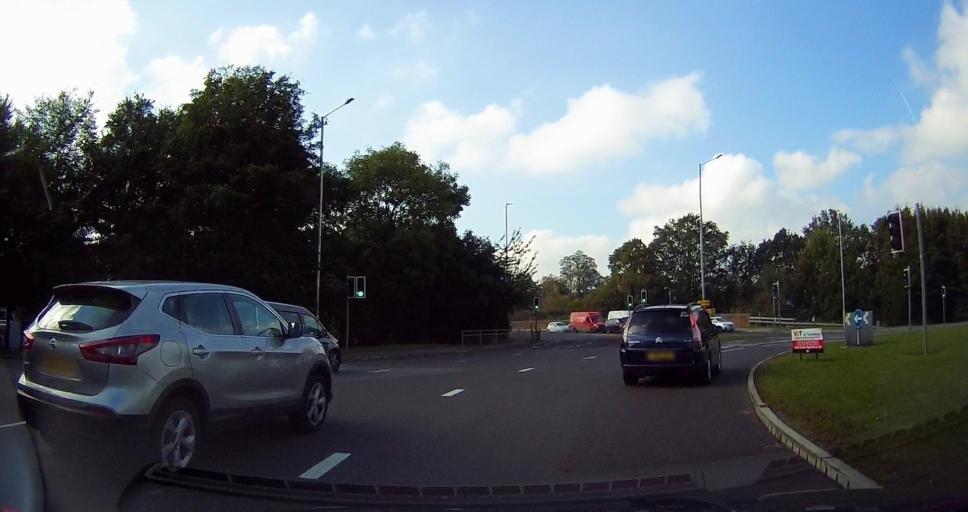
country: GB
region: England
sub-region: Kent
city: Ashford
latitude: 51.1567
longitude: 0.8607
